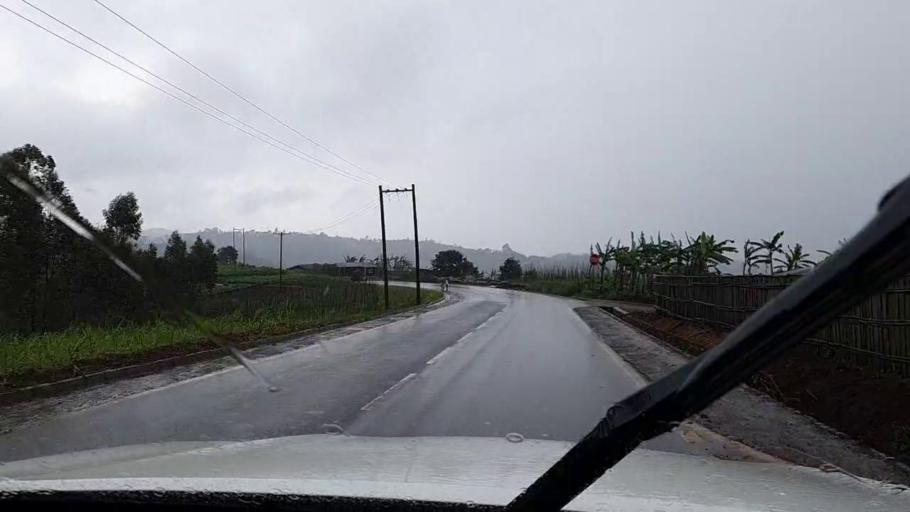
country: RW
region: Western Province
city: Cyangugu
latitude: -2.4620
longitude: 28.9886
